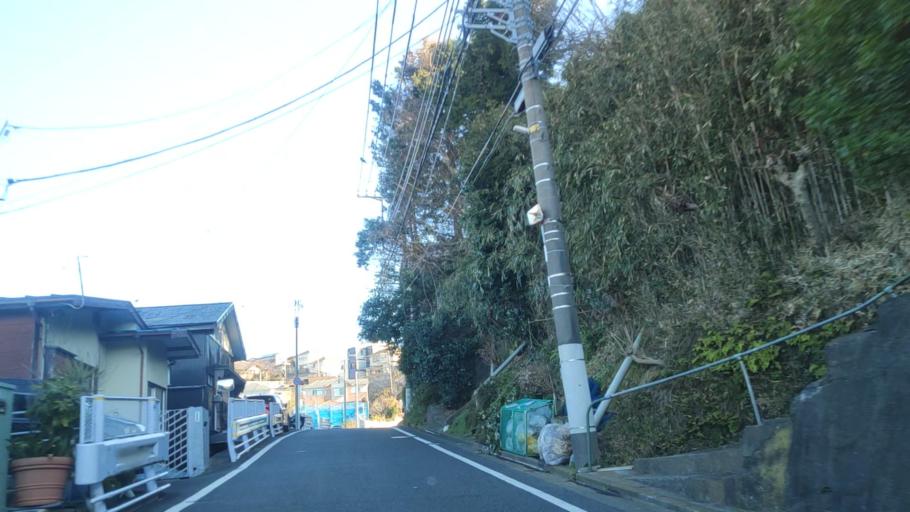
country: JP
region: Kanagawa
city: Yokohama
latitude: 35.4485
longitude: 139.5803
